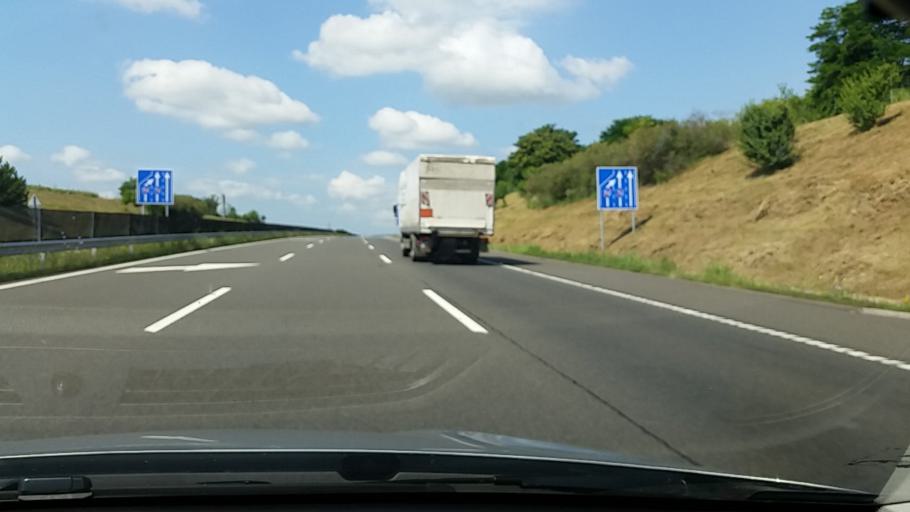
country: HU
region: Baranya
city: Kozarmisleny
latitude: 46.0152
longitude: 18.2582
